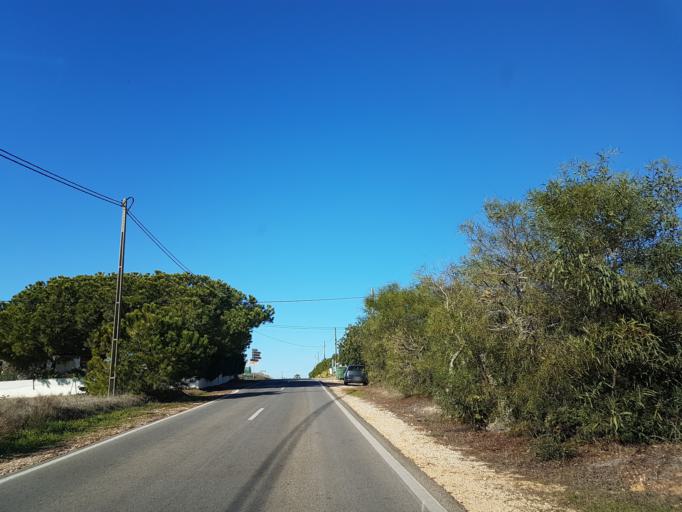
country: PT
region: Faro
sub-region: Lagoa
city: Carvoeiro
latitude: 37.0969
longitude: -8.4394
